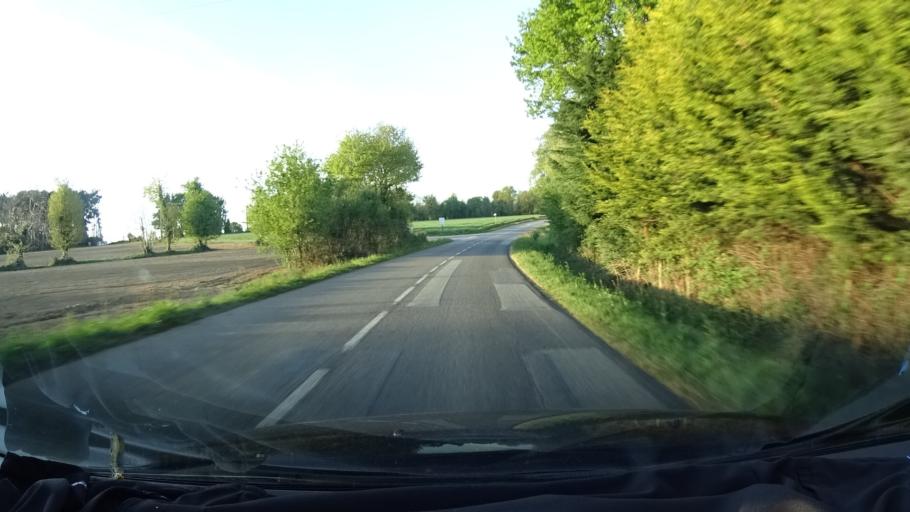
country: FR
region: Brittany
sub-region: Departement du Morbihan
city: Peaule
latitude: 47.5874
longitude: -2.3432
